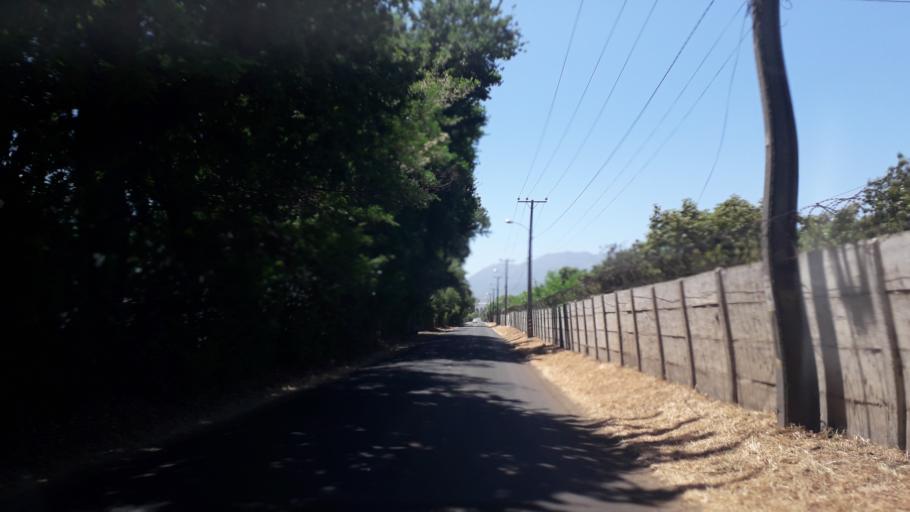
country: CL
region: Valparaiso
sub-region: Provincia de Quillota
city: Quillota
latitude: -32.9267
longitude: -71.2505
